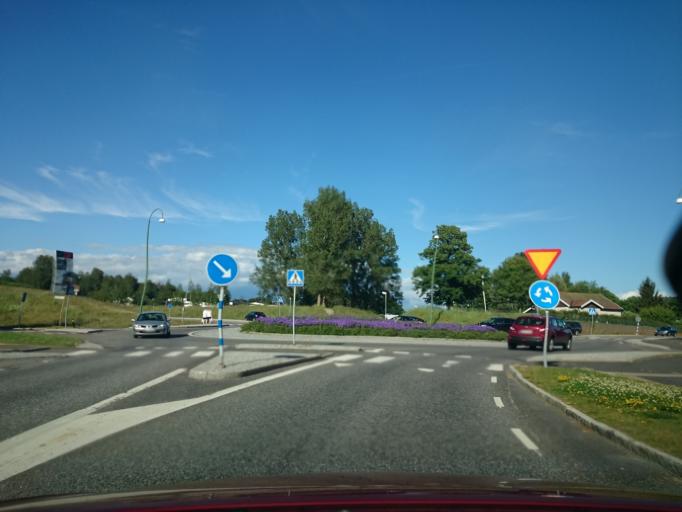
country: SE
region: Vaestra Goetaland
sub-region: Lerums Kommun
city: Lerum
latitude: 57.7771
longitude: 12.2780
